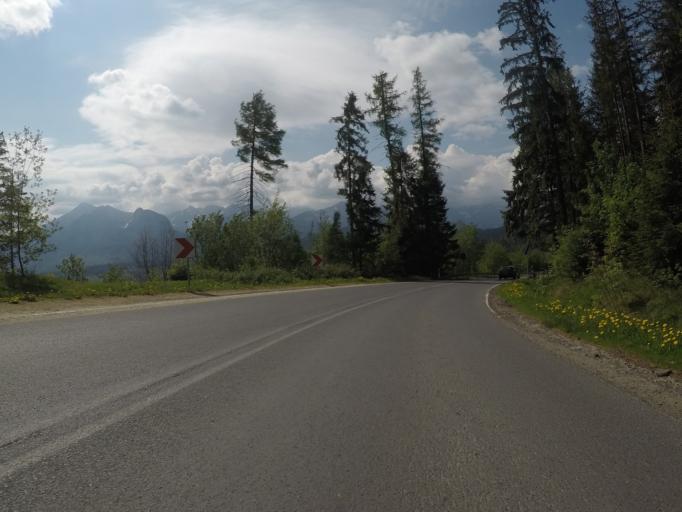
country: PL
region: Lesser Poland Voivodeship
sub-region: Powiat tatrzanski
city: Bukowina Tatrzanska
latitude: 49.3008
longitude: 20.1184
